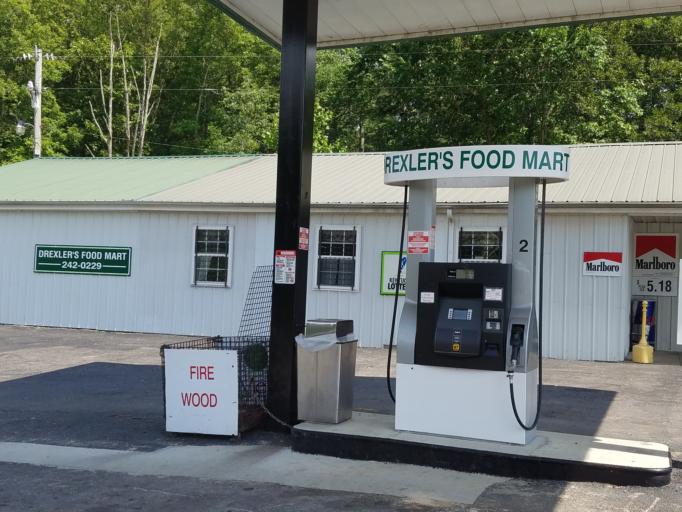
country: US
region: Kentucky
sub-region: Grayson County
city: Leitchfield
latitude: 37.3512
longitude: -86.1296
